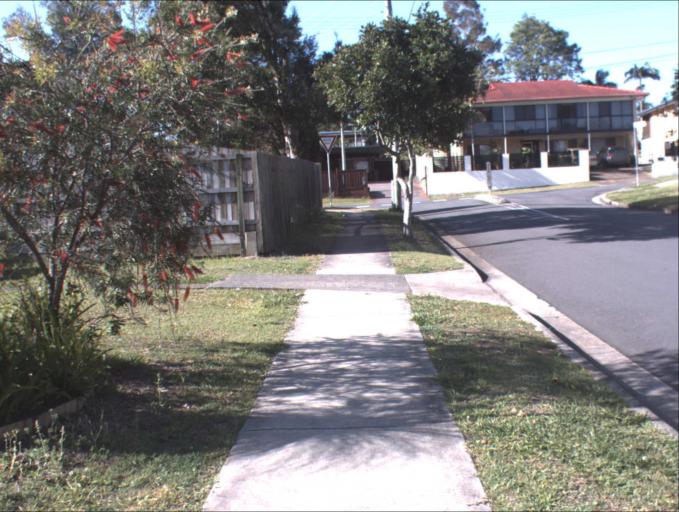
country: AU
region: Queensland
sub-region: Logan
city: Rochedale South
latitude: -27.6017
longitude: 153.1177
